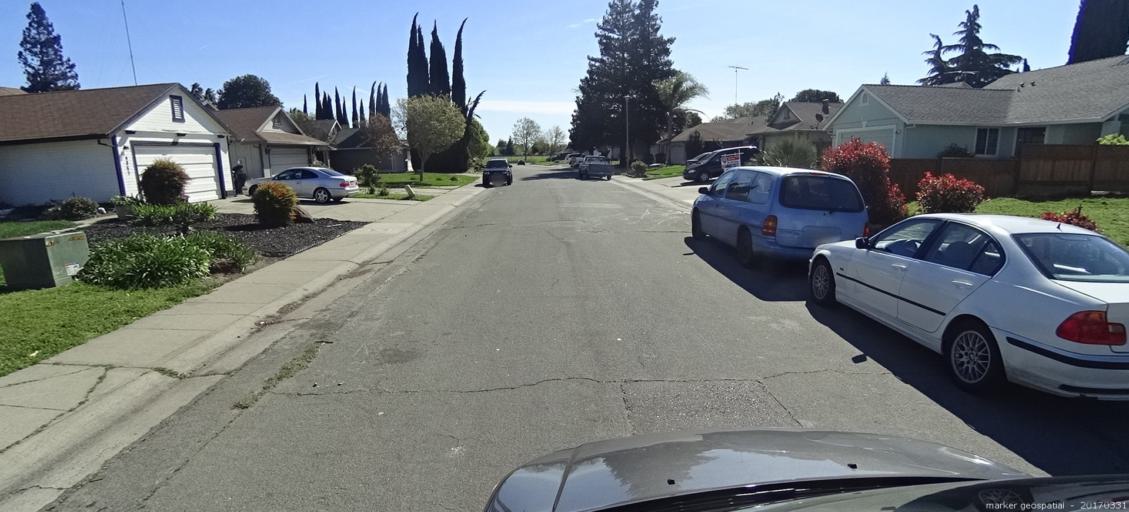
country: US
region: California
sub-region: Sacramento County
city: Parkway
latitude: 38.4682
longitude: -121.4440
